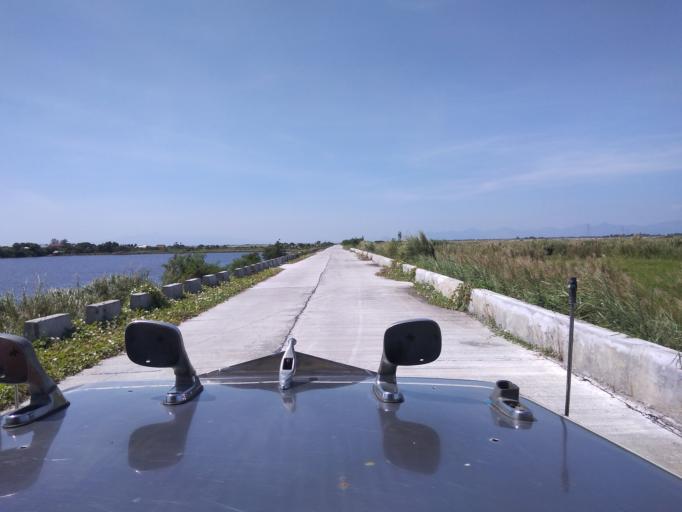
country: PH
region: Central Luzon
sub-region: Province of Pampanga
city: Minalin
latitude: 14.9839
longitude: 120.6919
